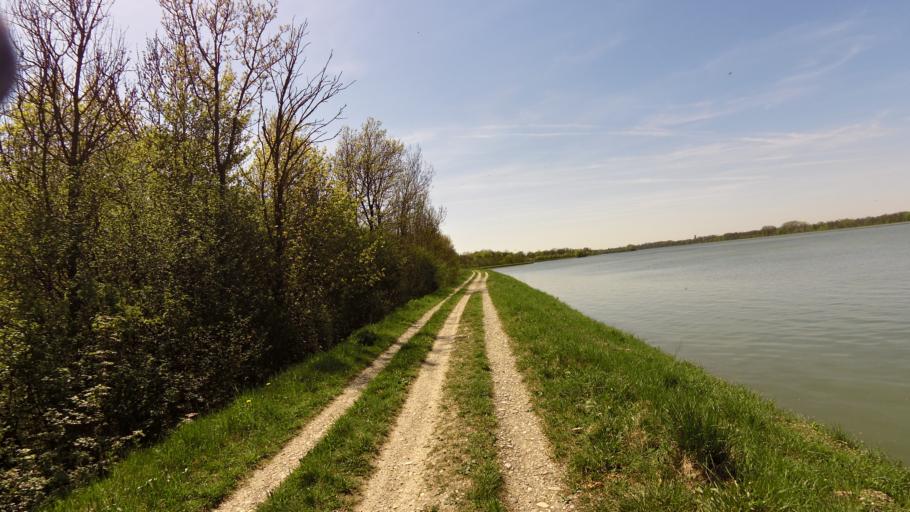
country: DE
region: Bavaria
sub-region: Lower Bavaria
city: Stallwang
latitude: 48.5757
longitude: 12.2165
